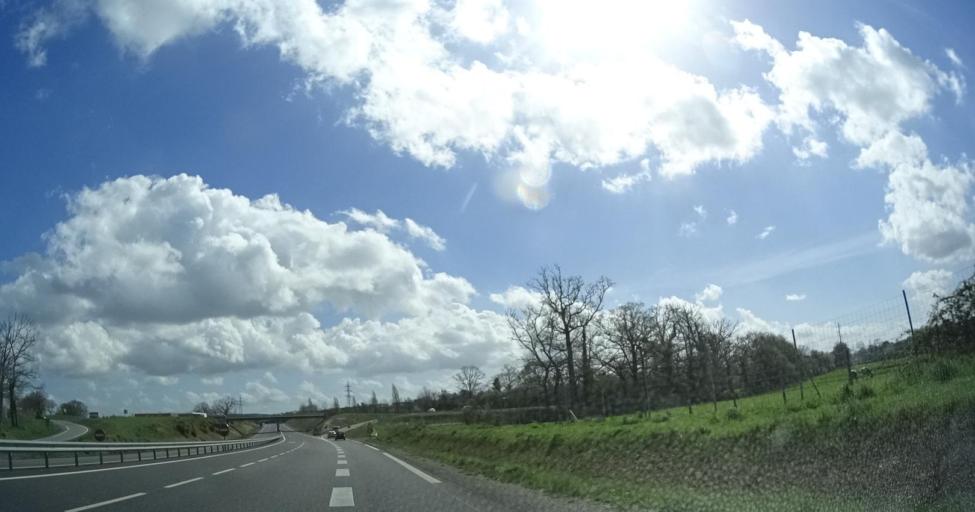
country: FR
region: Brittany
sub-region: Departement d'Ille-et-Vilaine
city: Bains-sur-Oust
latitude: 47.6784
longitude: -2.0648
